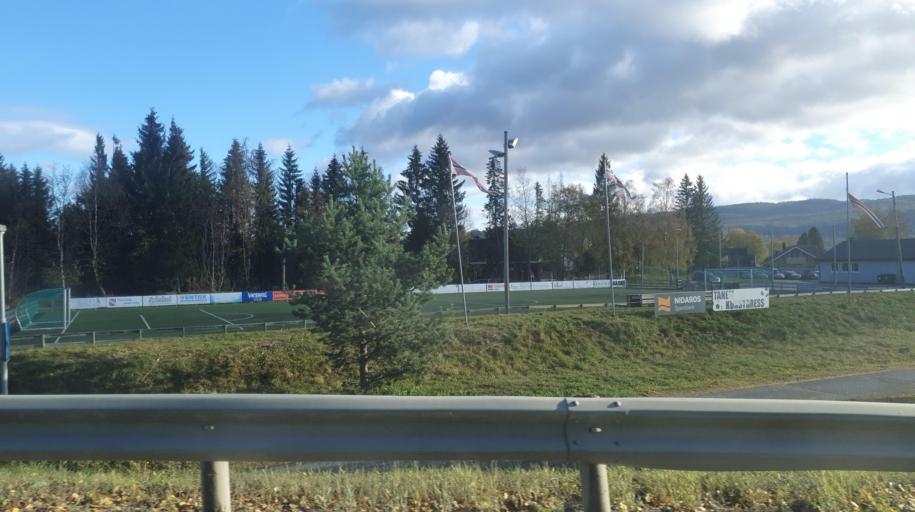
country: NO
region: Sor-Trondelag
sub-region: Klaebu
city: Klaebu
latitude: 63.3071
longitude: 10.4323
